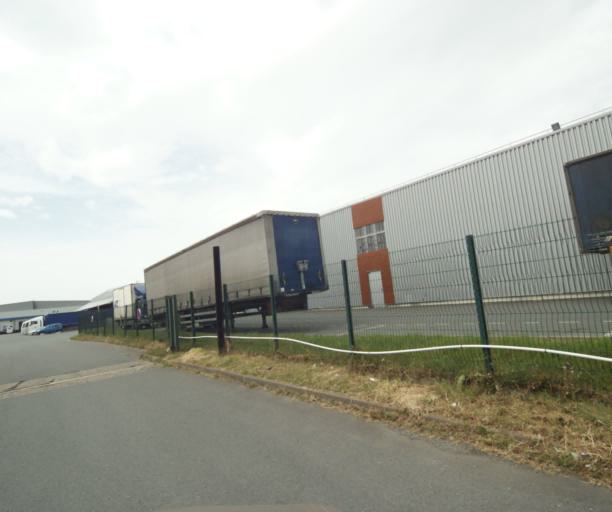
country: FR
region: Aquitaine
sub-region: Departement des Pyrenees-Atlantiques
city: Mouguerre
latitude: 43.4868
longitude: -1.4260
